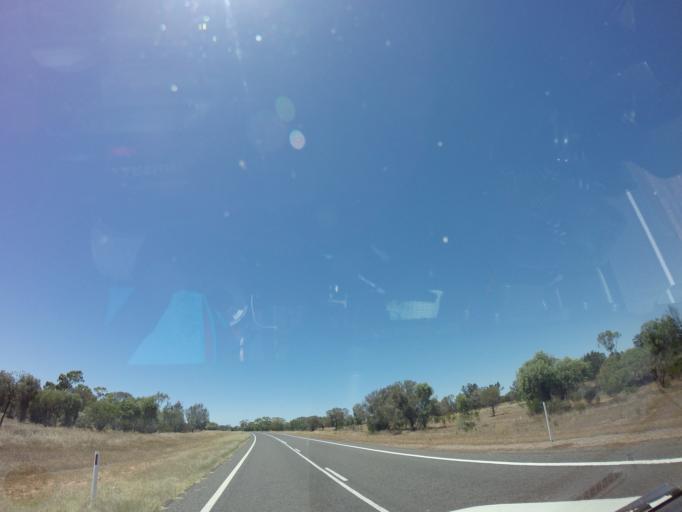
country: AU
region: New South Wales
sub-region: Cobar
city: Cobar
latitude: -31.5756
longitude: 144.7999
